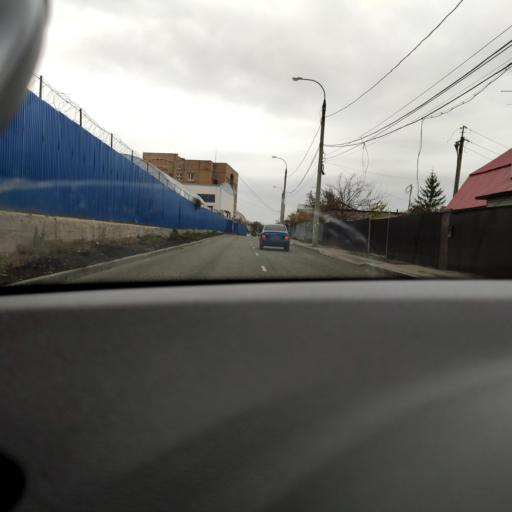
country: RU
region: Samara
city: Samara
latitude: 53.1796
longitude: 50.1403
